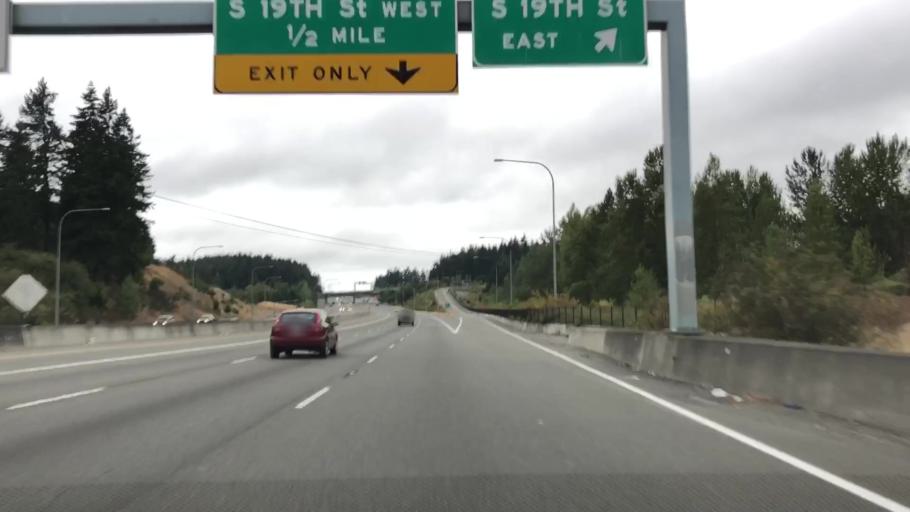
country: US
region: Washington
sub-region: Pierce County
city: Fircrest
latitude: 47.2374
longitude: -122.5002
